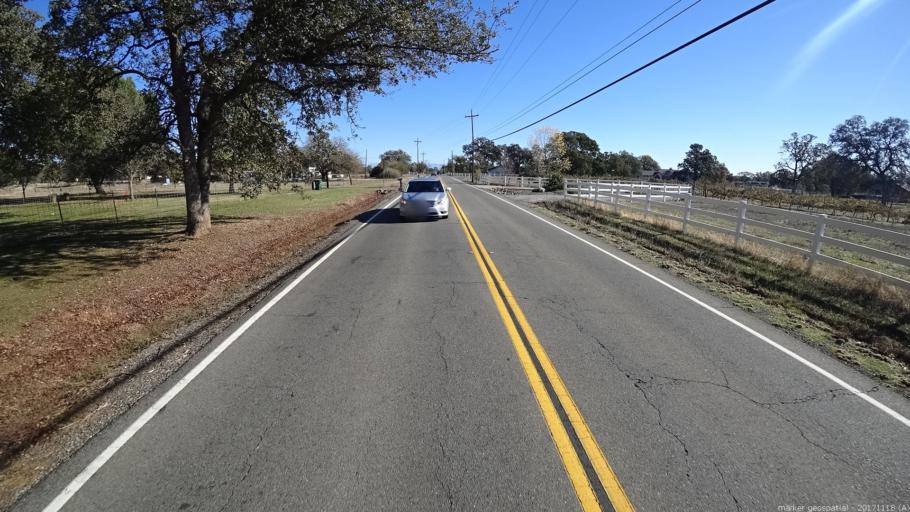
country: US
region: California
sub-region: Shasta County
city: Cottonwood
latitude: 40.3896
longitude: -122.3585
